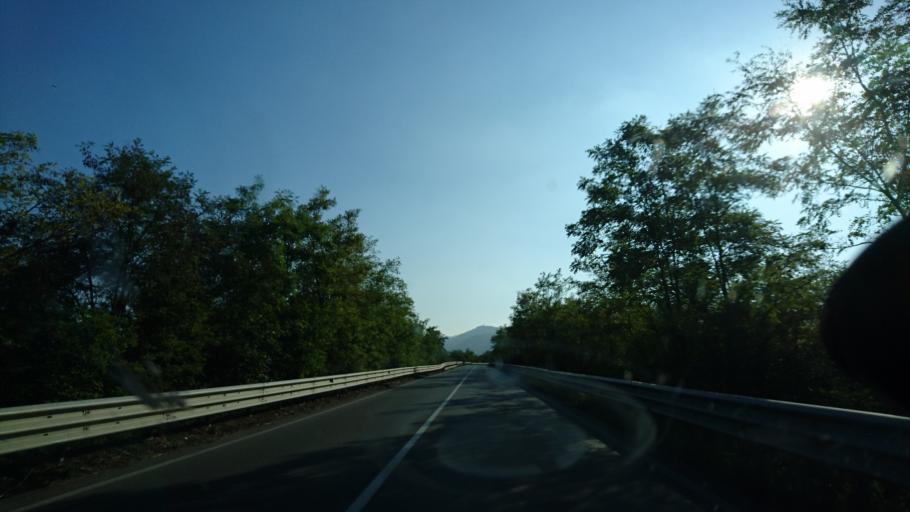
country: IT
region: Piedmont
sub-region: Provincia di Alessandria
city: Terzo
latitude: 44.6713
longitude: 8.4274
